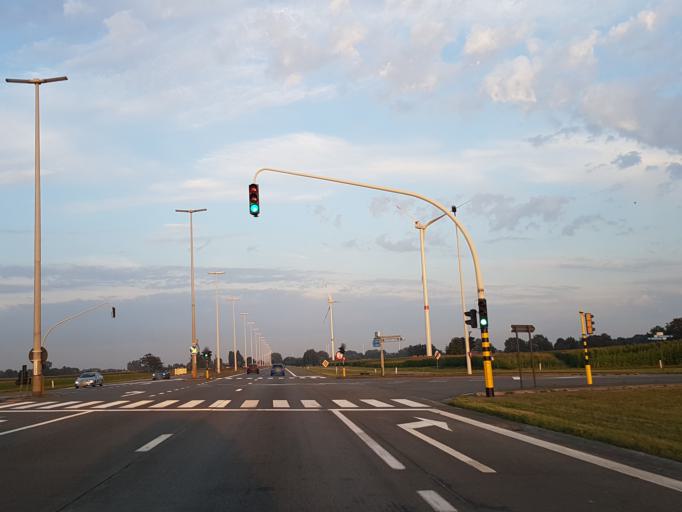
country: BE
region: Flanders
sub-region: Provincie Oost-Vlaanderen
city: Assenede
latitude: 51.2036
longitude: 3.7072
